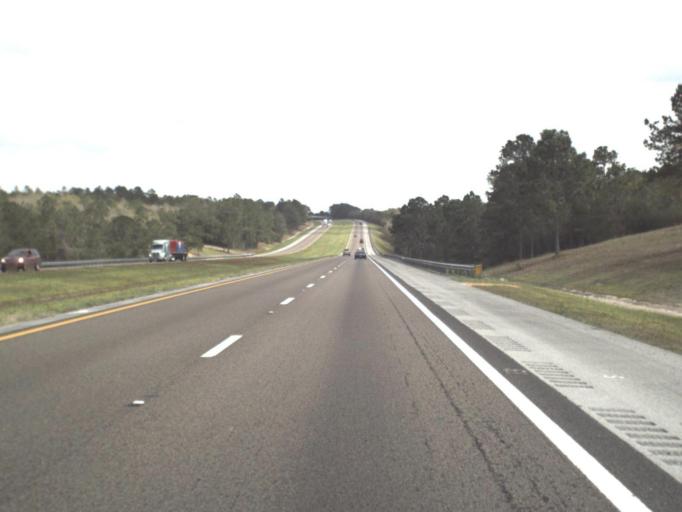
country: US
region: Florida
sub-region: Walton County
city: DeFuniak Springs
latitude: 30.7353
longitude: -86.2216
